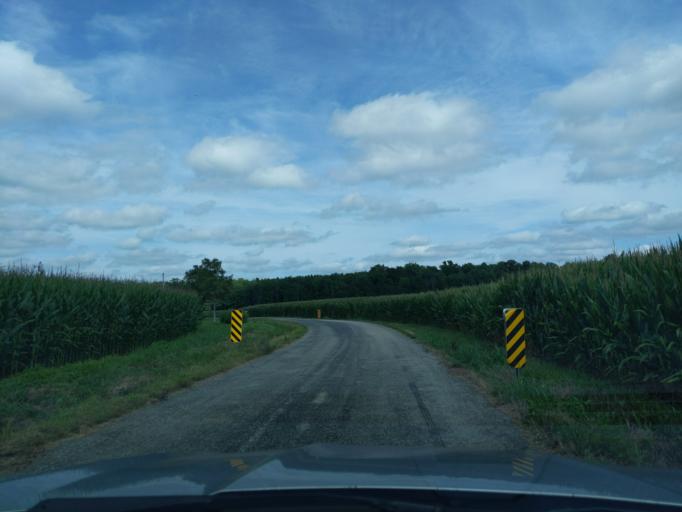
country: US
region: Indiana
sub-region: Ripley County
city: Osgood
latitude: 39.2355
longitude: -85.3615
